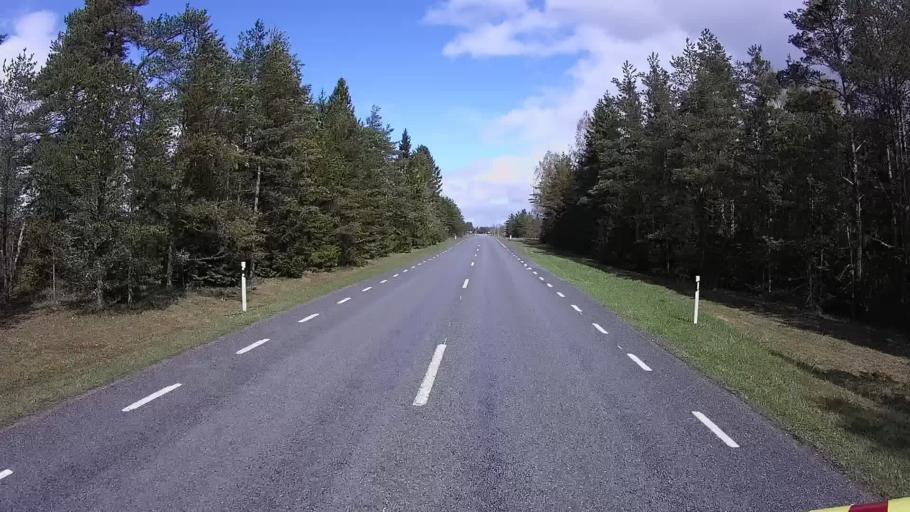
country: EE
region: Hiiumaa
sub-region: Kaerdla linn
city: Kardla
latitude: 58.9499
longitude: 22.7718
